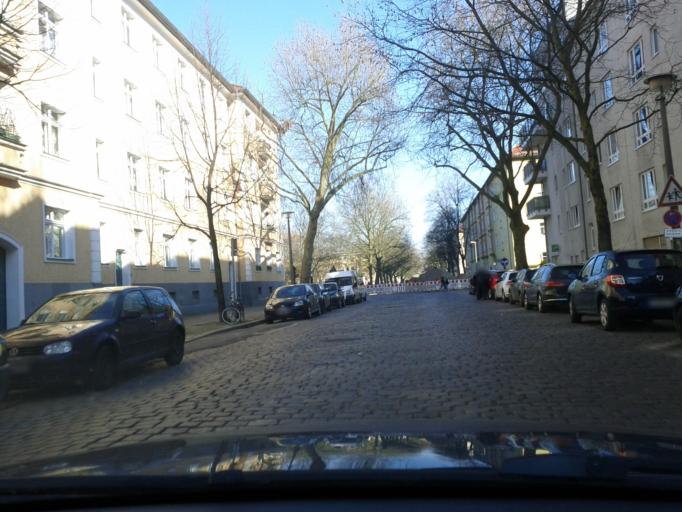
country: DE
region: Berlin
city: Lichtenberg
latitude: 52.5156
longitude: 13.4992
